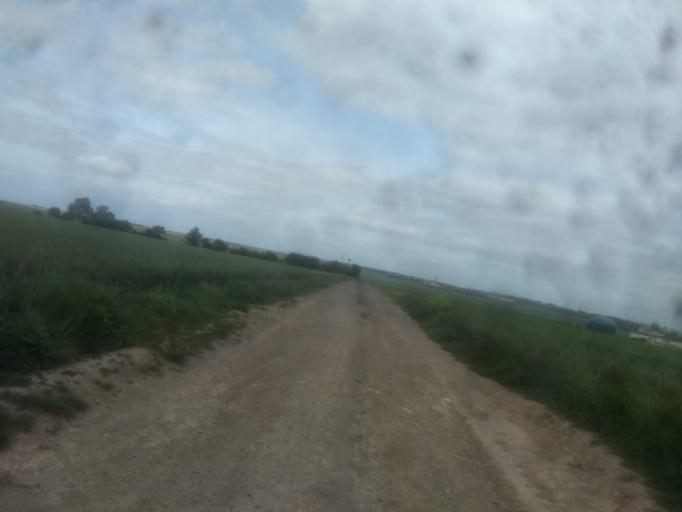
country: FR
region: Nord-Pas-de-Calais
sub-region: Departement du Pas-de-Calais
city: Tilloy-les-Mofflaines
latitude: 50.2827
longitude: 2.8248
